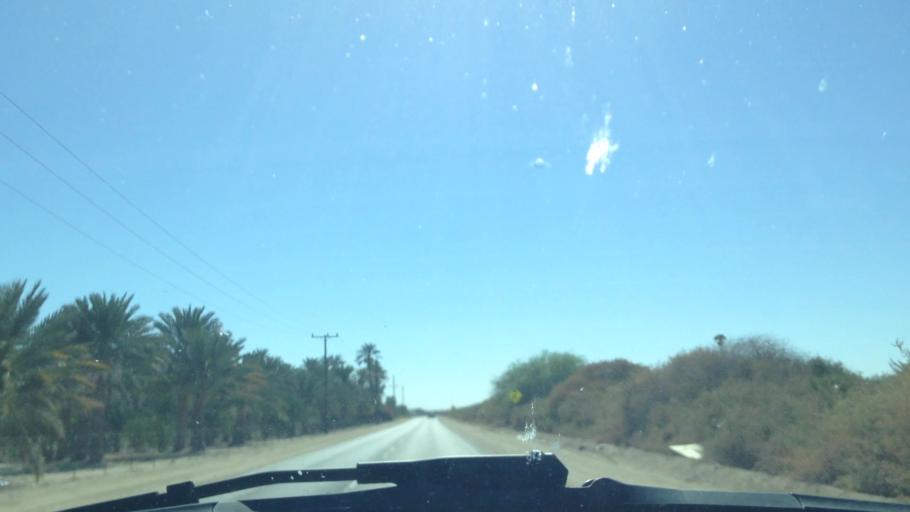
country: US
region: California
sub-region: Riverside County
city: Mecca
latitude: 33.5422
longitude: -116.0333
